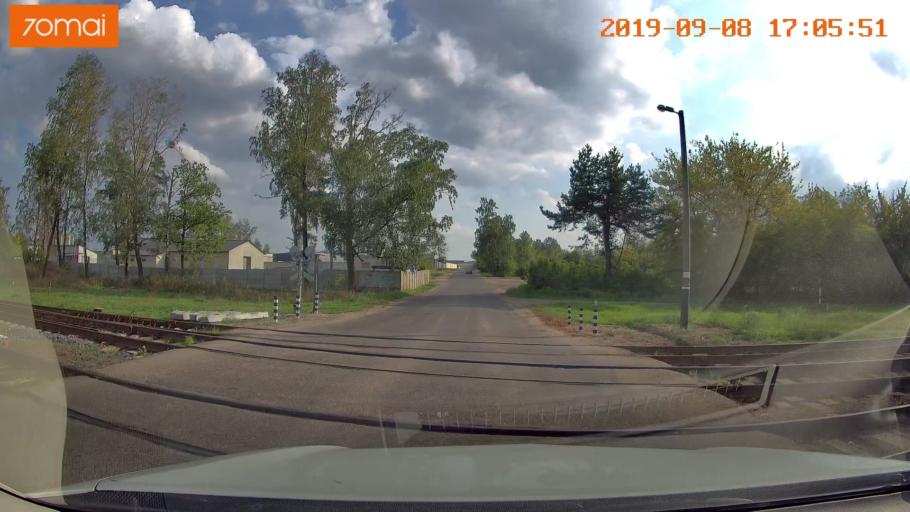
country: BY
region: Grodnenskaya
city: Hrodna
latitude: 53.6751
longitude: 23.9534
